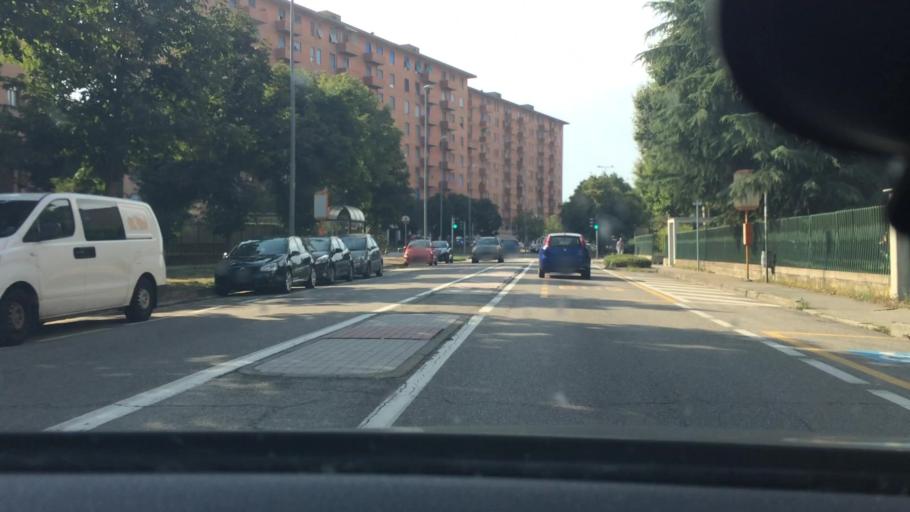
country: IT
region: Lombardy
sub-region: Citta metropolitana di Milano
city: Settimo Milanese
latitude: 45.4824
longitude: 9.0583
